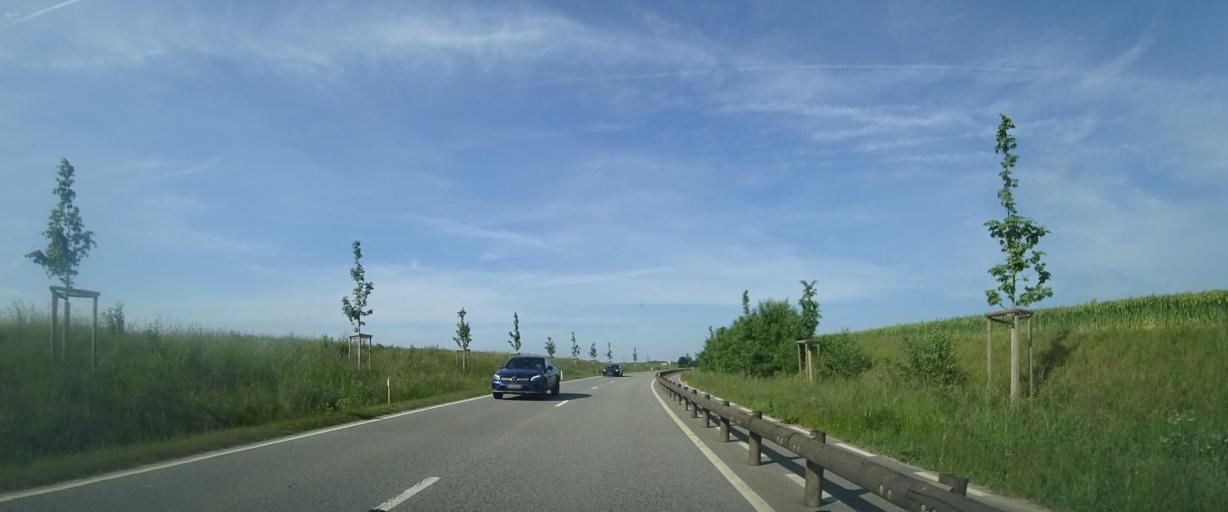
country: BE
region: Wallonia
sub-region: Province du Brabant Wallon
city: Chaumont-Gistoux
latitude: 50.6552
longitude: 4.7376
